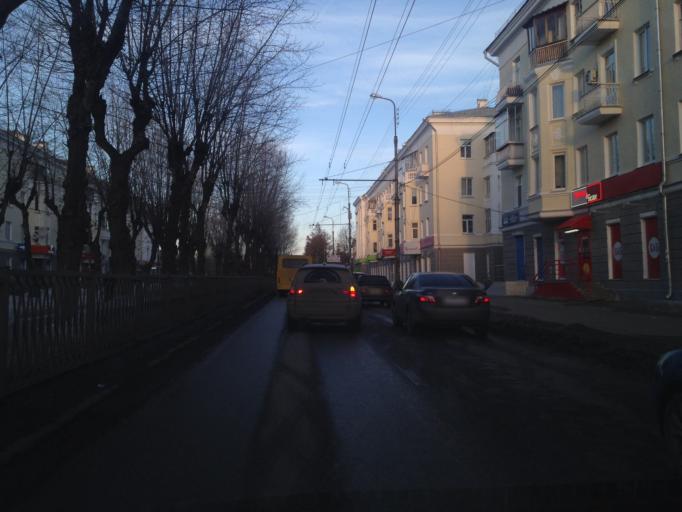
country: RU
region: Sverdlovsk
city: Istok
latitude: 56.7552
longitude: 60.7050
